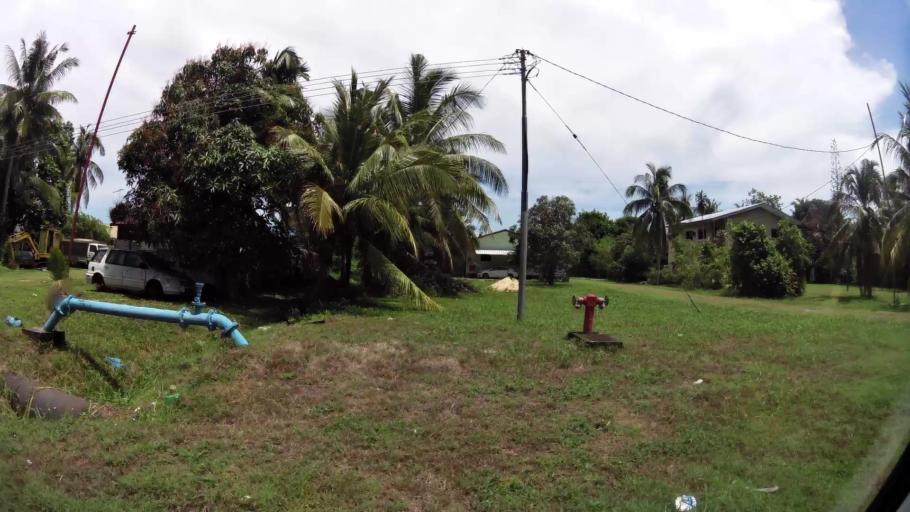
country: BN
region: Belait
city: Kuala Belait
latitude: 4.5845
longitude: 114.2488
